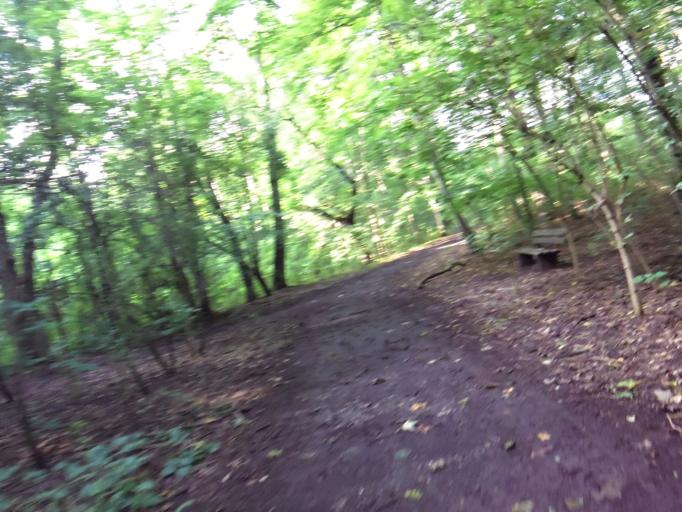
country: DE
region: Saxony
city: Leipzig
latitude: 51.3099
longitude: 12.3415
